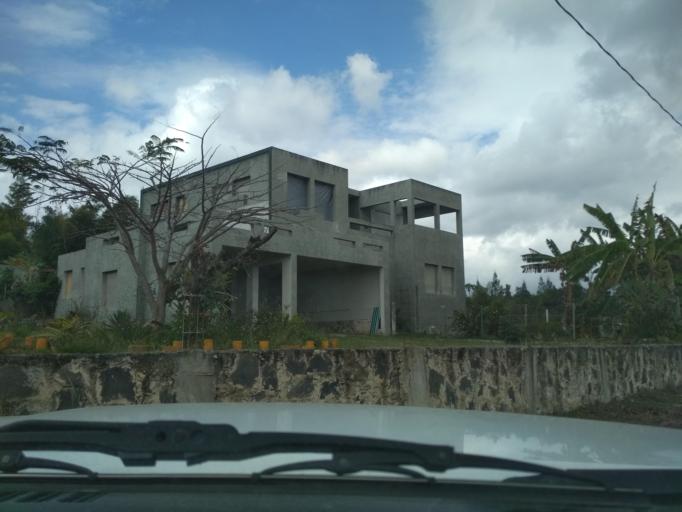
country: MX
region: Veracruz
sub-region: Emiliano Zapata
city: Dos Rios
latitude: 19.5018
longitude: -96.8229
